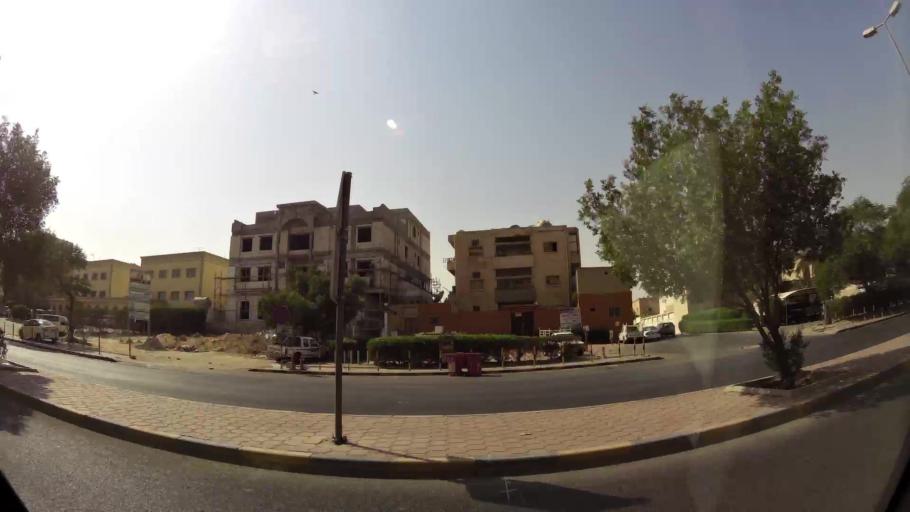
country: KW
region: Al Ahmadi
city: Al Fahahil
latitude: 29.0819
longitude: 48.1229
